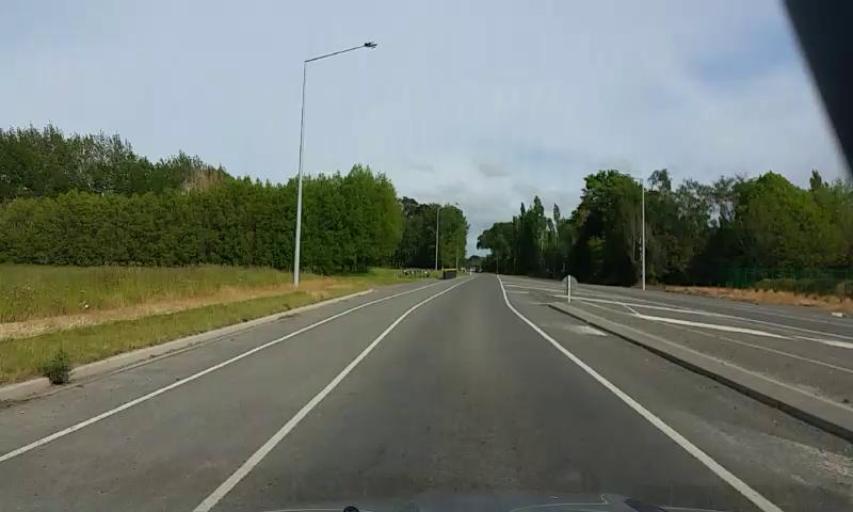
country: NZ
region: Canterbury
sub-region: Selwyn District
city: Prebbleton
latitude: -43.5180
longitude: 172.5263
